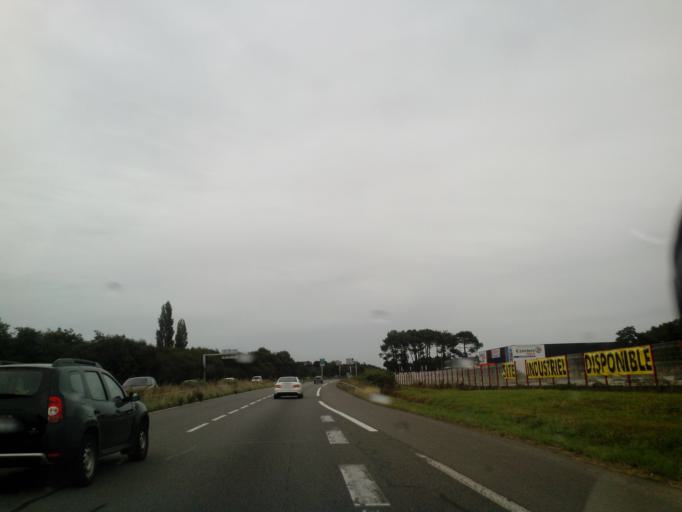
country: FR
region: Brittany
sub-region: Departement du Finistere
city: Redene
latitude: 47.8473
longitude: -3.5065
